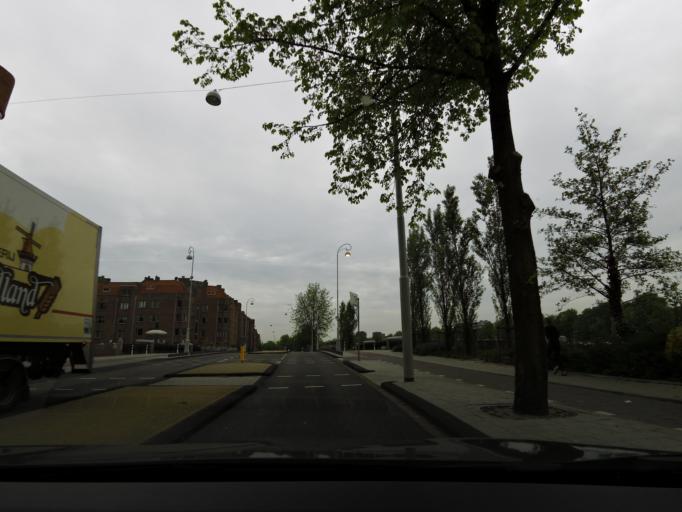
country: NL
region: North Holland
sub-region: Gemeente Amsterdam
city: Amsterdam
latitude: 52.3494
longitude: 4.9099
